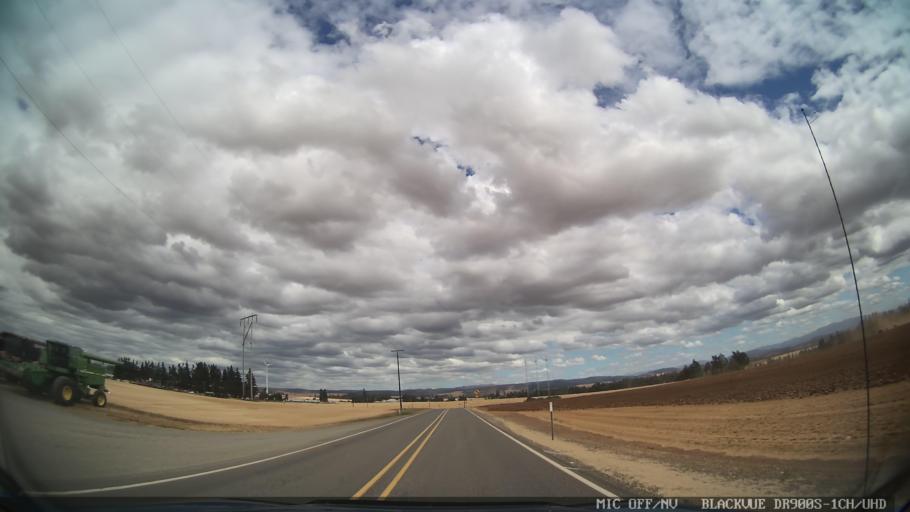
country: US
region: Oregon
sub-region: Marion County
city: Sublimity
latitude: 44.8653
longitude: -122.8139
